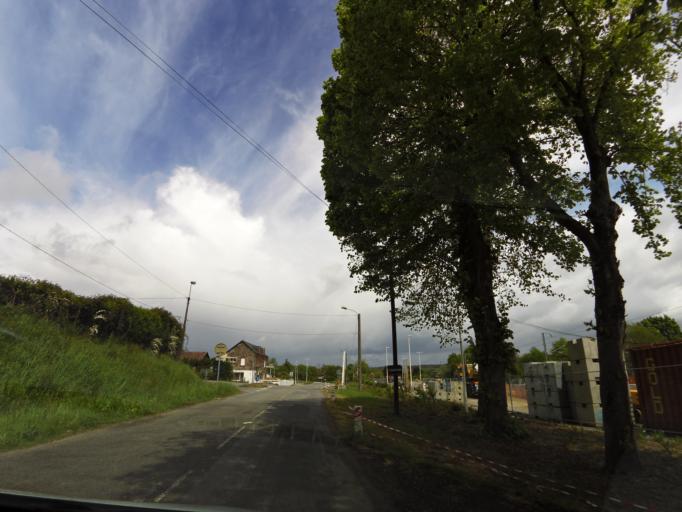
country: FR
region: Brittany
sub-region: Departement d'Ille-et-Vilaine
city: Bourg-des-Comptes
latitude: 47.9354
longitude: -1.7604
